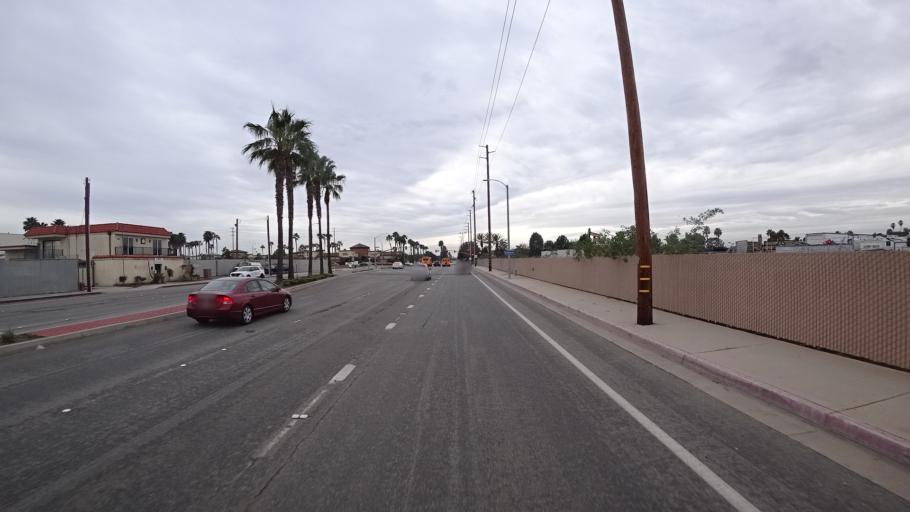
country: US
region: California
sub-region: Orange County
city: Huntington Beach
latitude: 33.6866
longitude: -118.0045
